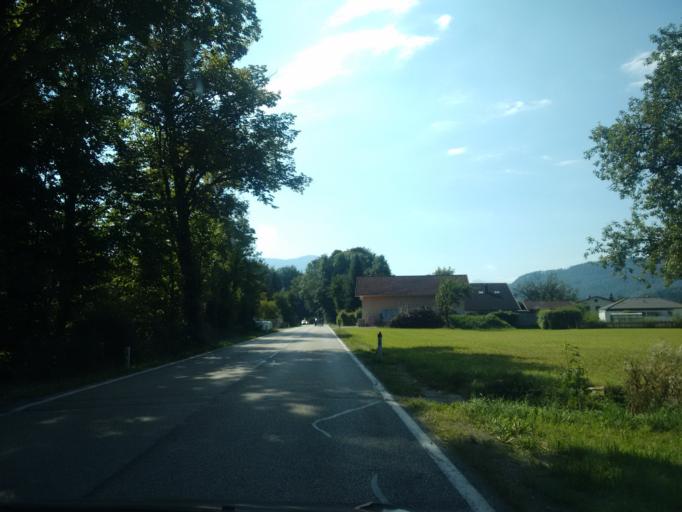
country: AT
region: Upper Austria
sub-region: Politischer Bezirk Gmunden
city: Gruenau im Almtal
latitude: 47.8796
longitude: 13.9406
